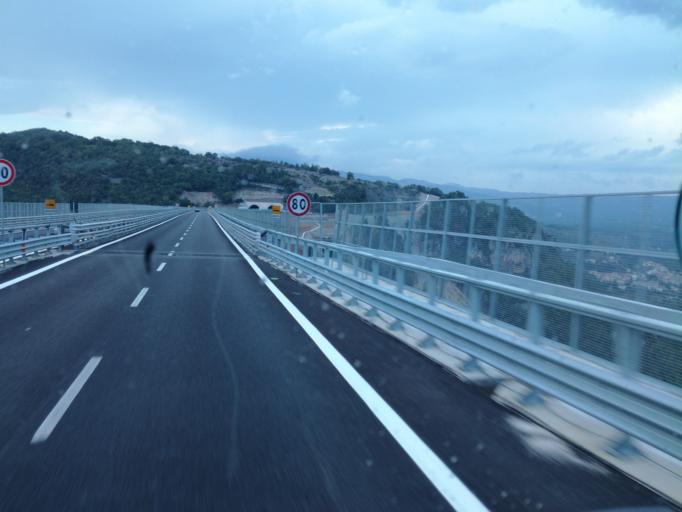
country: IT
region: Calabria
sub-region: Provincia di Cosenza
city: Laino Castello-Nuovo Centro
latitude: 39.9373
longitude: 15.9601
